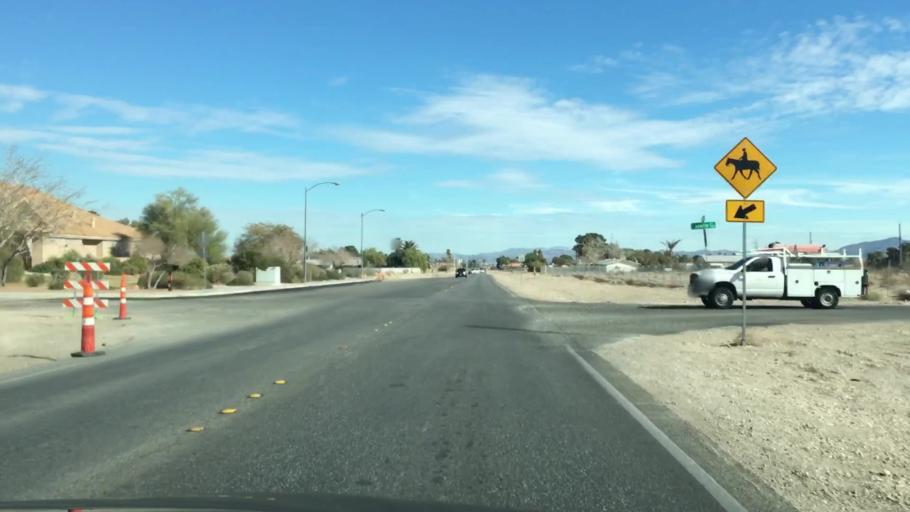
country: US
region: Nevada
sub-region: Clark County
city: Enterprise
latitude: 36.0572
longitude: -115.1995
